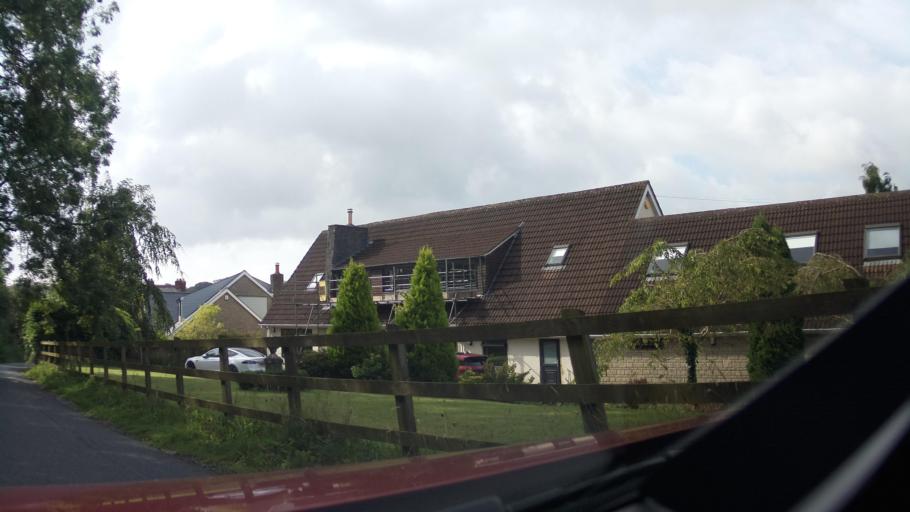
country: GB
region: England
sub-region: Somerset
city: Shepton Mallet
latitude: 51.2260
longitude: -2.5349
